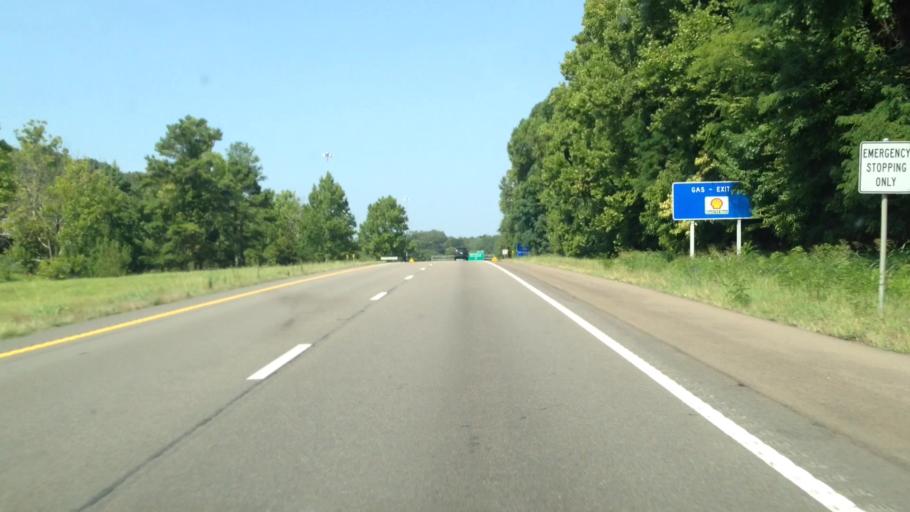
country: US
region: Mississippi
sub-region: Warren County
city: Vicksburg
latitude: 32.3123
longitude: -90.8909
